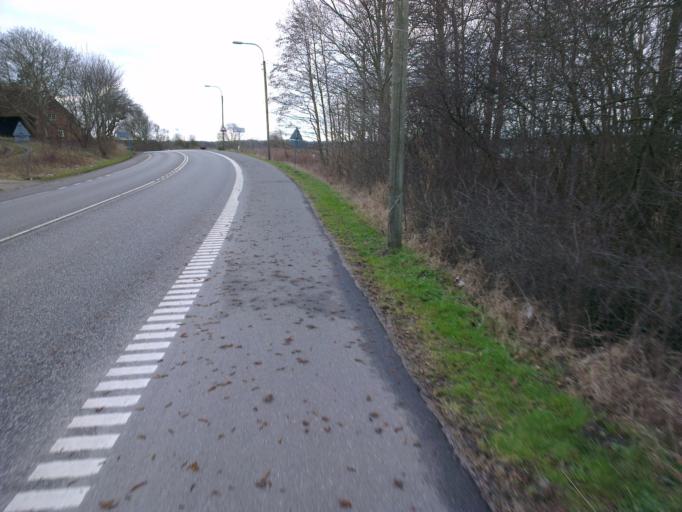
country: DK
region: Capital Region
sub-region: Frederikssund Kommune
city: Jaegerspris
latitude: 55.8547
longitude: 12.0152
